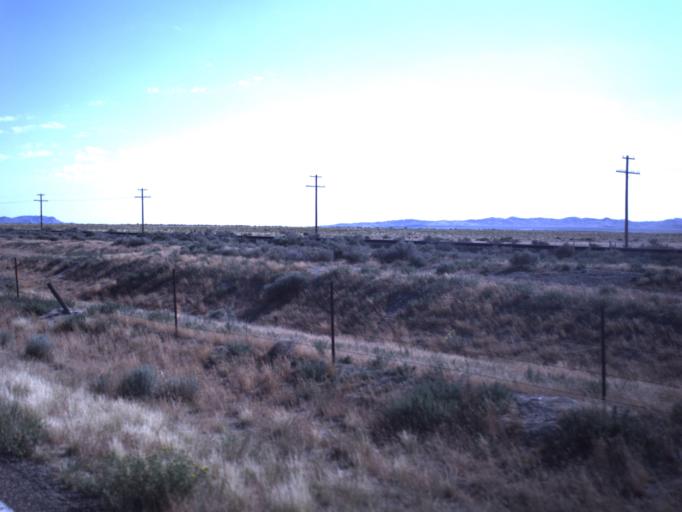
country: US
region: Utah
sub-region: Beaver County
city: Milford
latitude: 38.6546
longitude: -112.9820
